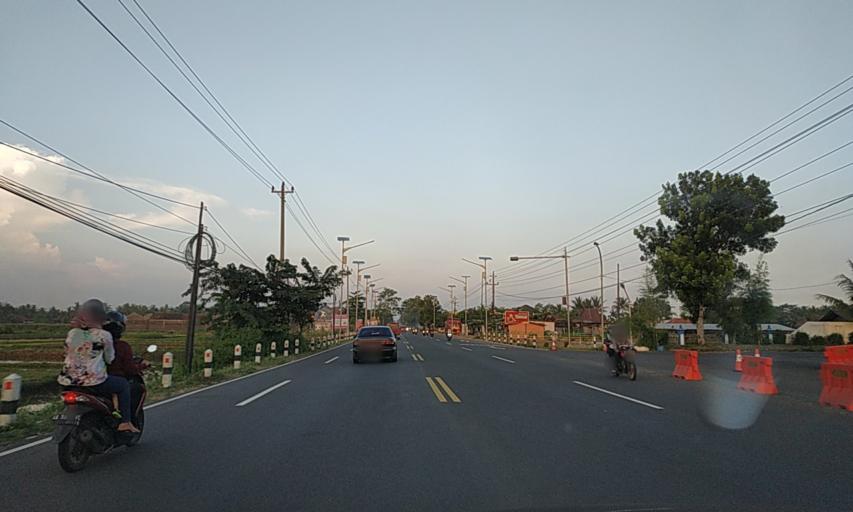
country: ID
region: Daerah Istimewa Yogyakarta
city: Srandakan
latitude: -7.8913
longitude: 110.1223
